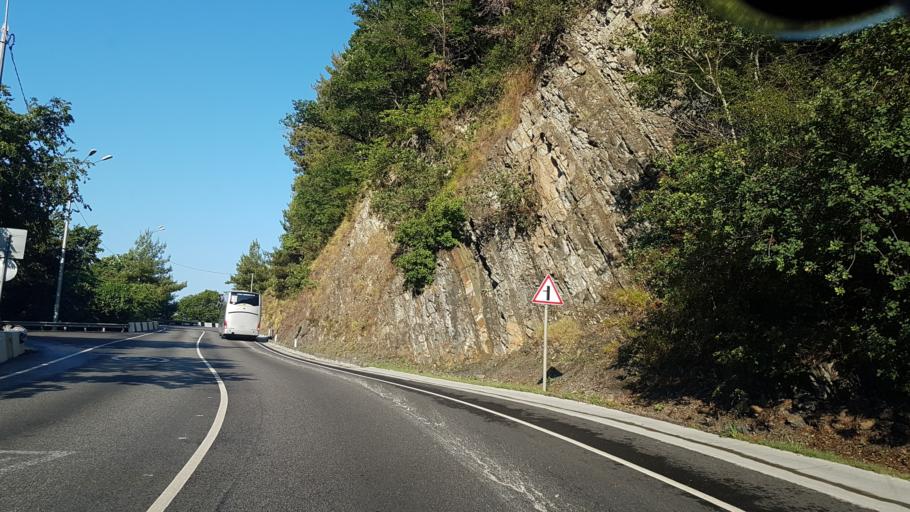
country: RU
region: Krasnodarskiy
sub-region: Sochi City
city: Lazarevskoye
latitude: 43.8391
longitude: 39.4201
